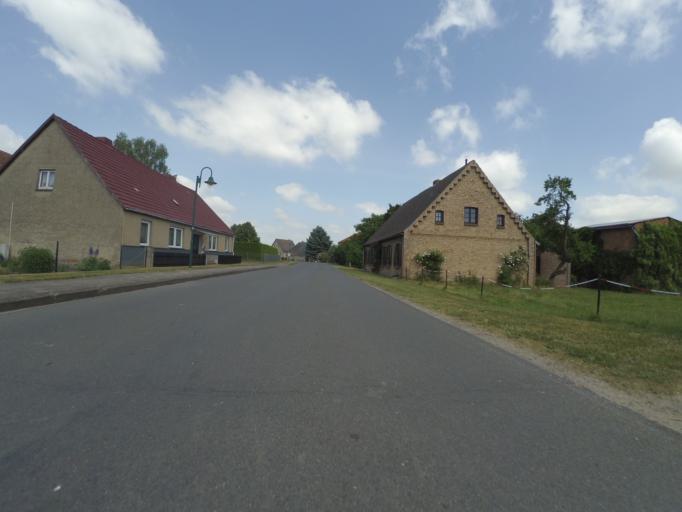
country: DE
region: Mecklenburg-Vorpommern
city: Lubz
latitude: 53.4034
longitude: 12.0137
